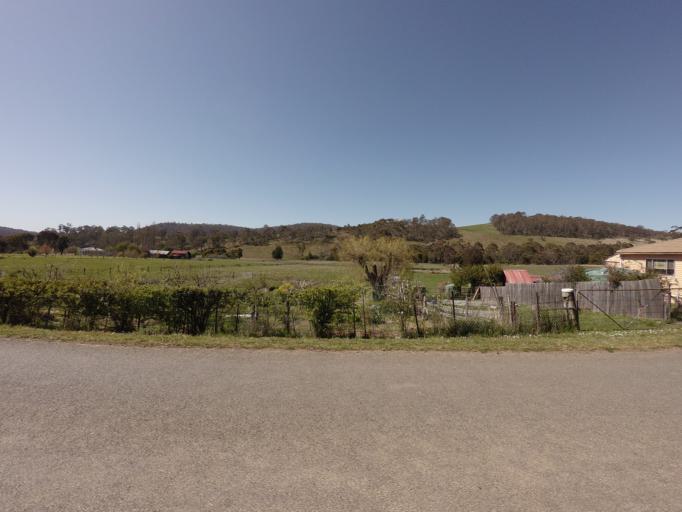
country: AU
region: Tasmania
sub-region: Derwent Valley
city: New Norfolk
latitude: -42.6196
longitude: 146.7173
